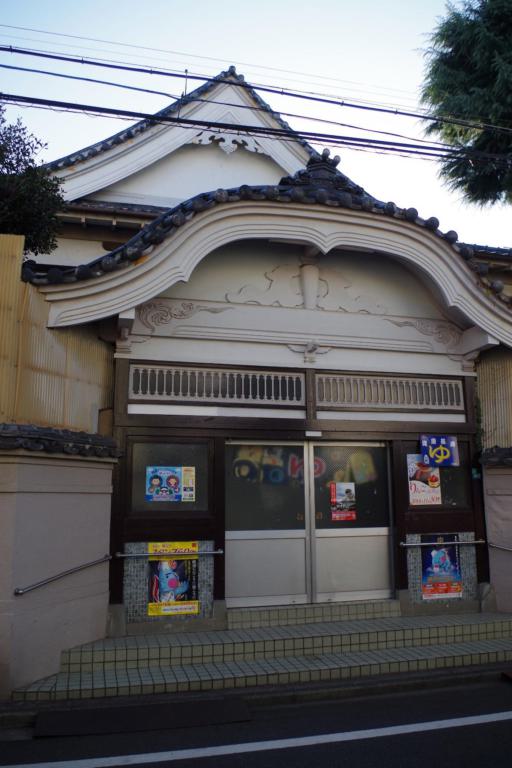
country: JP
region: Tokyo
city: Urayasu
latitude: 35.7052
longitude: 139.8485
